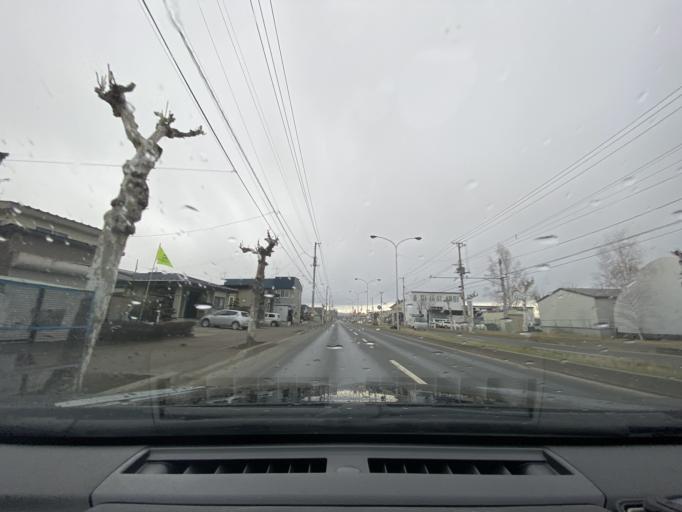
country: JP
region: Hokkaido
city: Kitami
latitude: 43.8013
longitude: 143.9028
